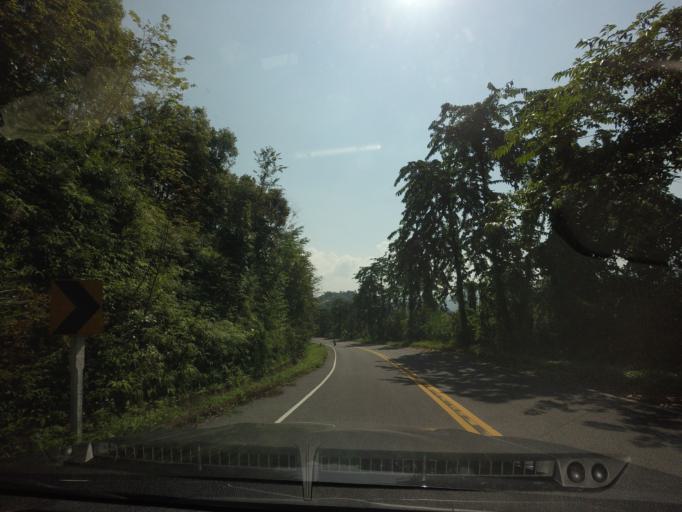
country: TH
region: Nan
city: Bo Kluea
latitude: 19.0334
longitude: 101.0839
